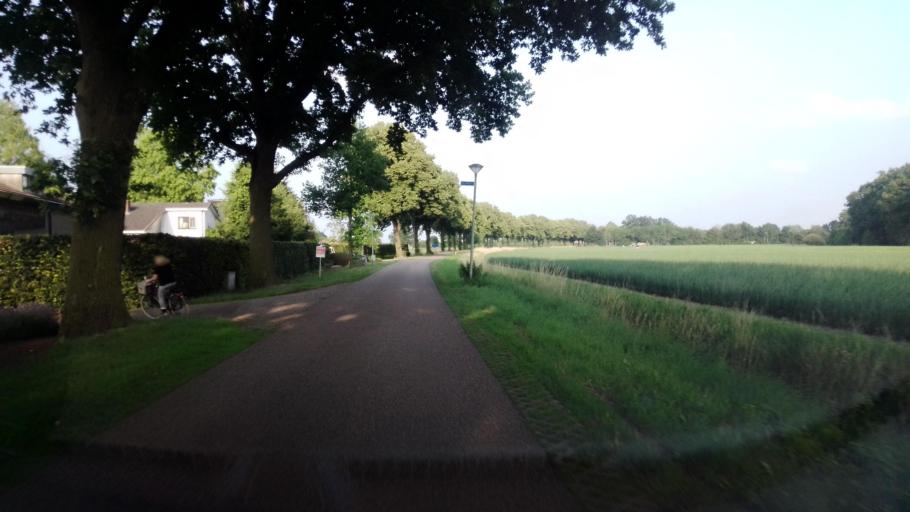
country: NL
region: Limburg
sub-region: Gemeente Peel en Maas
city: Maasbree
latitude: 51.4149
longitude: 6.0500
